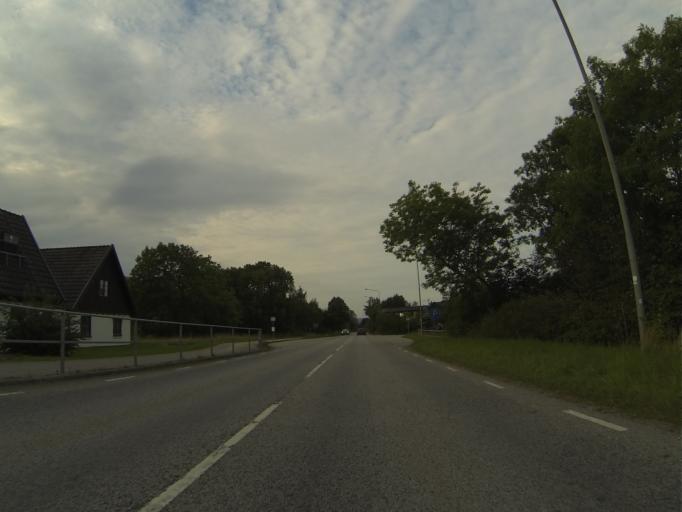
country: SE
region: Skane
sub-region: Lunds Kommun
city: Genarp
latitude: 55.7021
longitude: 13.3449
